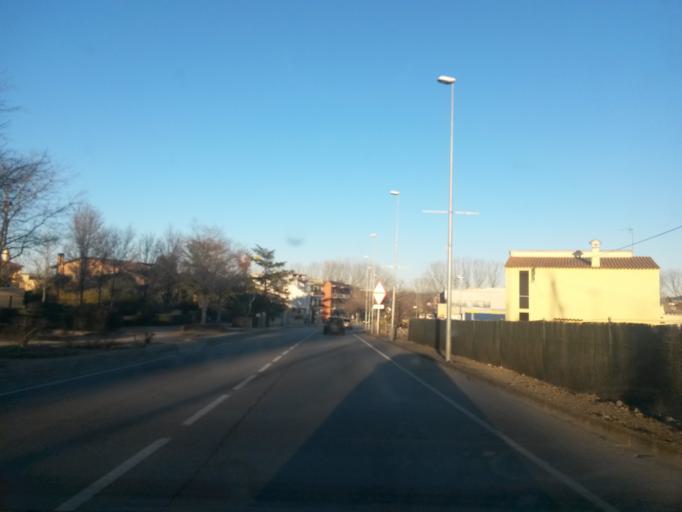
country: ES
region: Catalonia
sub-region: Provincia de Girona
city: Macanet de la Selva
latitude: 41.7792
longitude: 2.7371
